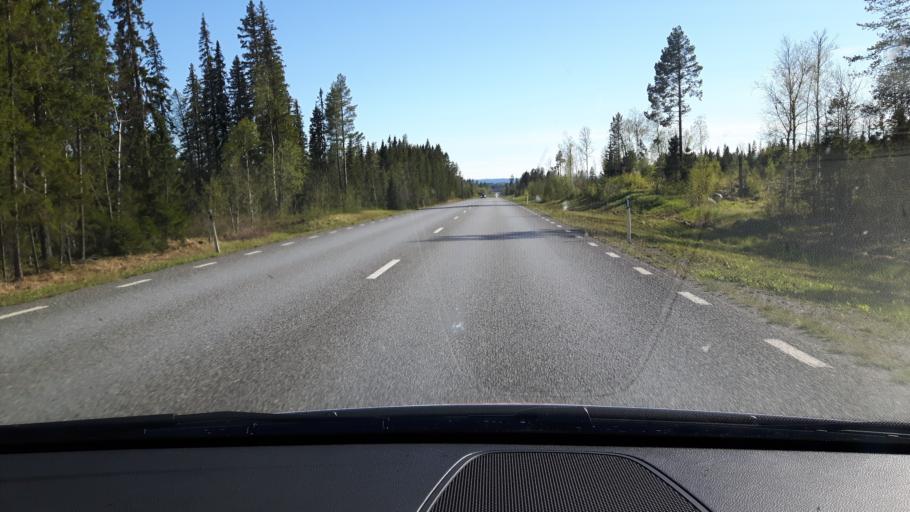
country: SE
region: Jaemtland
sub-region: Stroemsunds Kommun
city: Stroemsund
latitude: 63.7012
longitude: 15.4410
